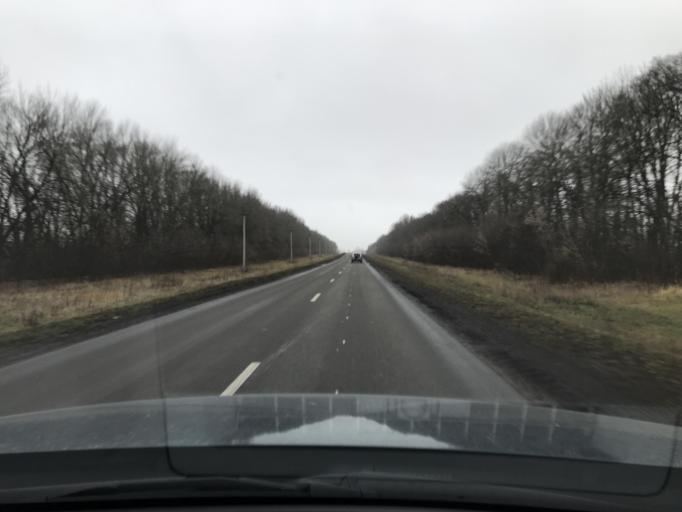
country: RU
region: Penza
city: Zemetchino
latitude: 53.5178
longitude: 42.6471
